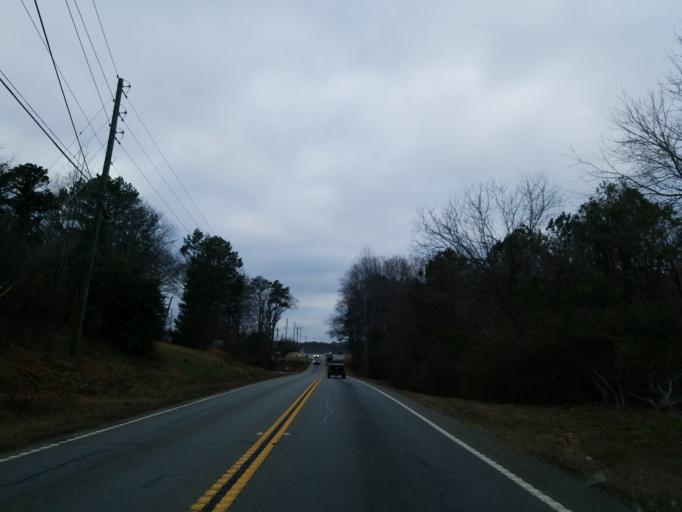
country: US
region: Georgia
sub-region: Cherokee County
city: Canton
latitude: 34.2707
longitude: -84.4982
